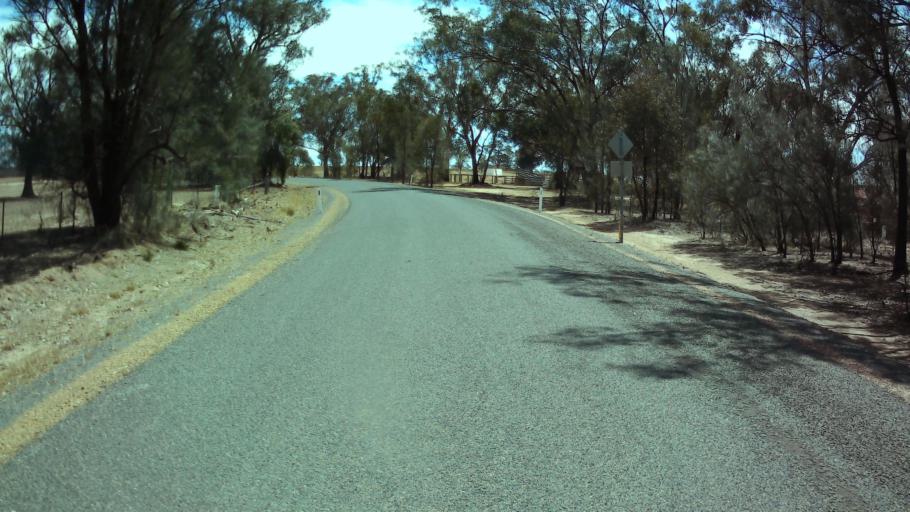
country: AU
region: New South Wales
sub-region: Weddin
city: Grenfell
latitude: -33.7385
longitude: 148.2091
